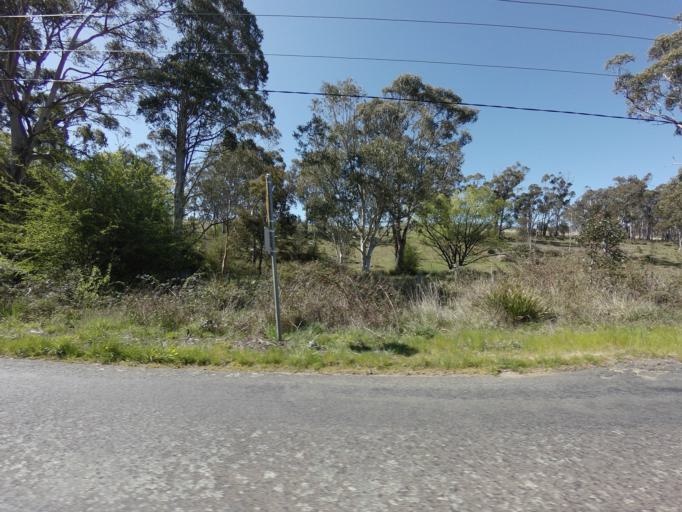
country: AU
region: Tasmania
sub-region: Derwent Valley
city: New Norfolk
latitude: -42.6272
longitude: 146.7248
